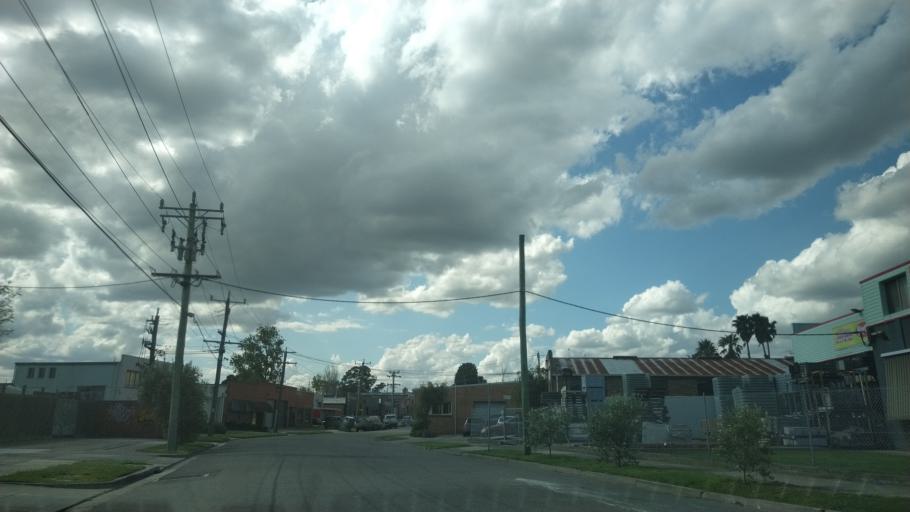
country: AU
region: Victoria
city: Highett
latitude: -37.9408
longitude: 145.0704
